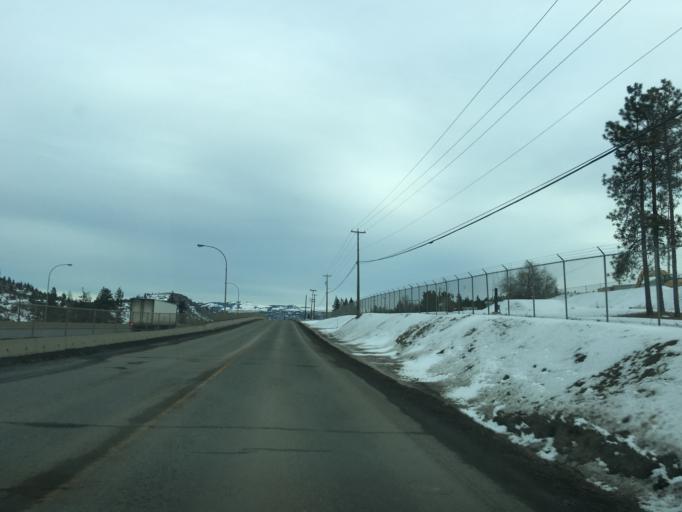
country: CA
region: British Columbia
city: Kamloops
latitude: 50.6646
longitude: -120.4151
